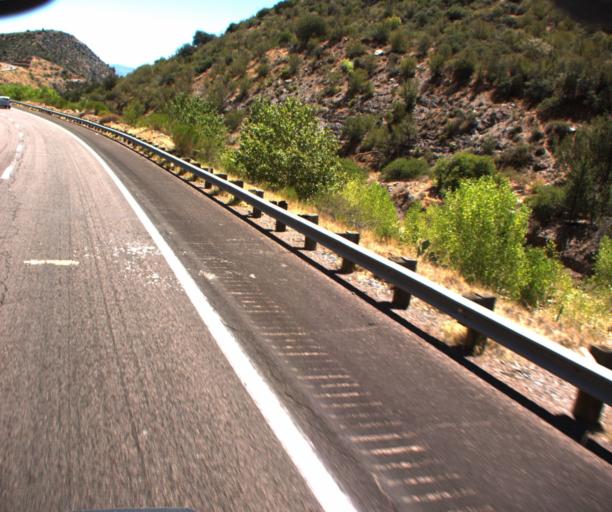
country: US
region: Arizona
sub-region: Gila County
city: Tonto Basin
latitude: 33.9589
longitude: -111.4024
